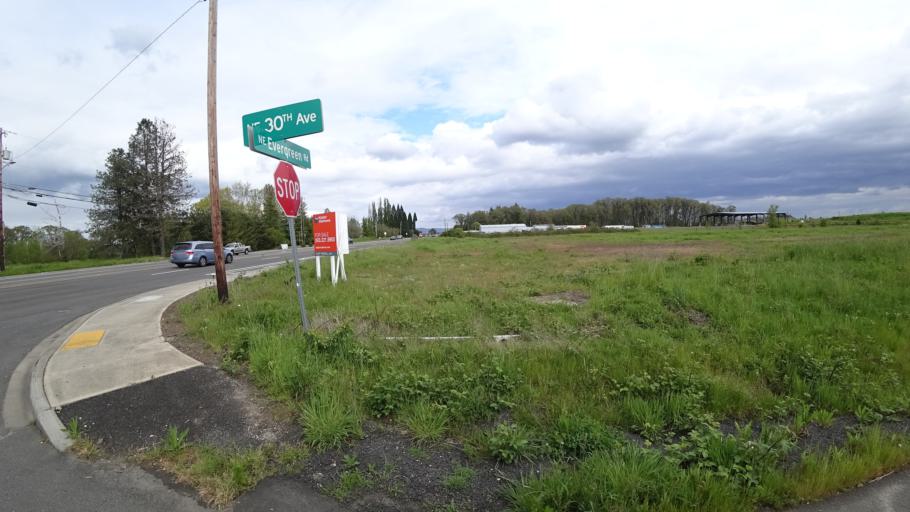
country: US
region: Oregon
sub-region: Washington County
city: Hillsboro
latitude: 45.5510
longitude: -122.9482
